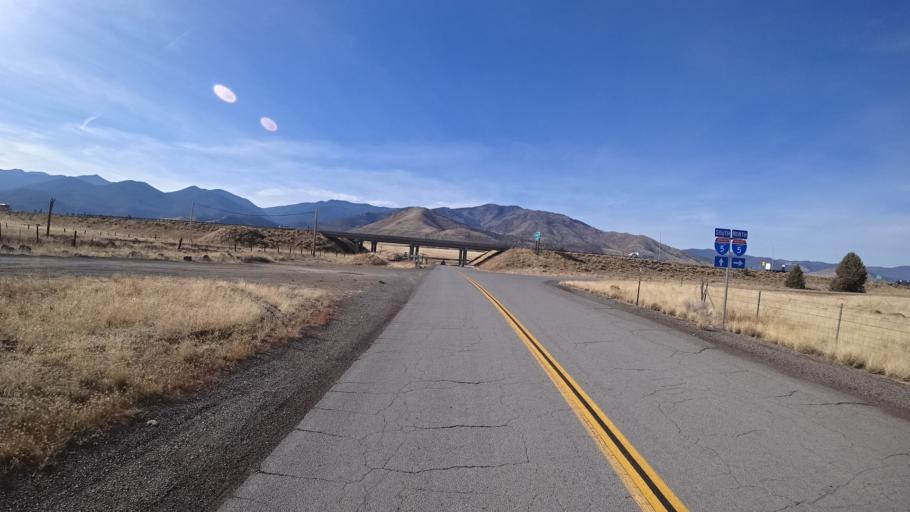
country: US
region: California
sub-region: Siskiyou County
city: Weed
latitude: 41.4720
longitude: -122.4501
